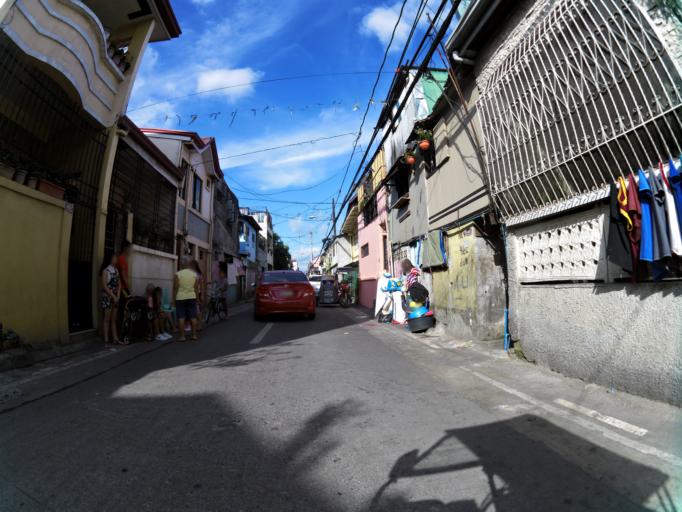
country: PH
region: Metro Manila
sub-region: Marikina
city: Calumpang
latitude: 14.6420
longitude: 121.0990
